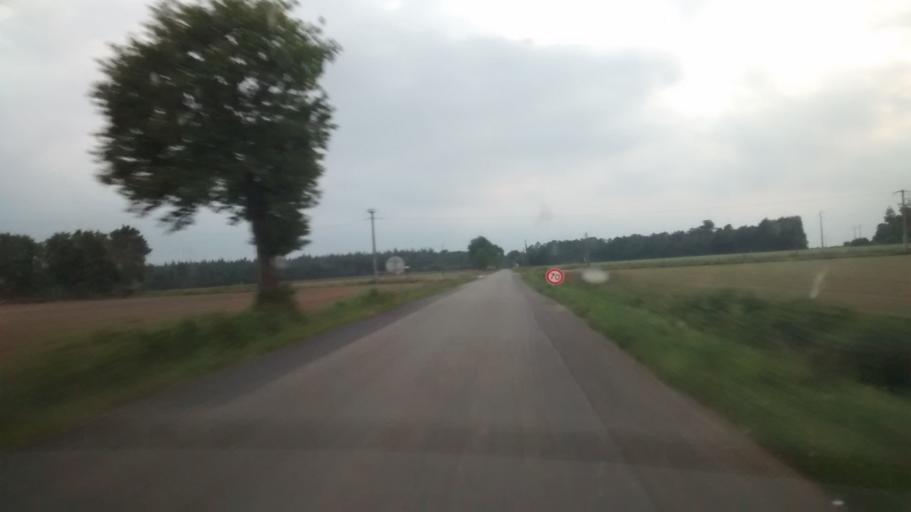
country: FR
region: Brittany
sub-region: Departement du Morbihan
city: Malansac
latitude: 47.7314
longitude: -2.3073
